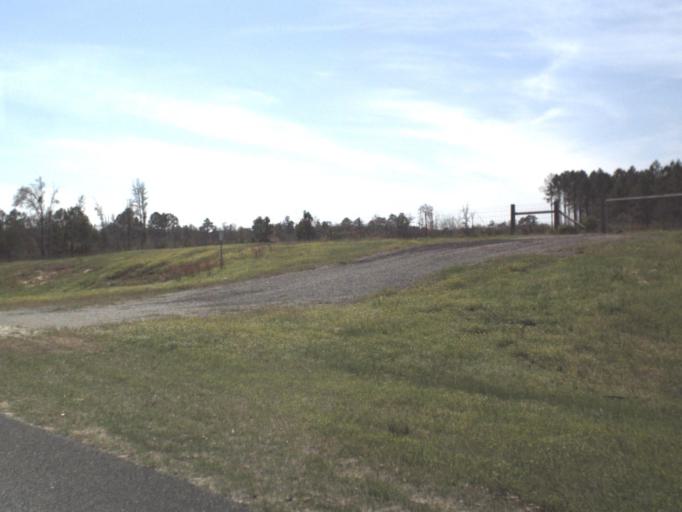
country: US
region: Florida
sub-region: Bay County
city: Lynn Haven
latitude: 30.4199
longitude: -85.6897
